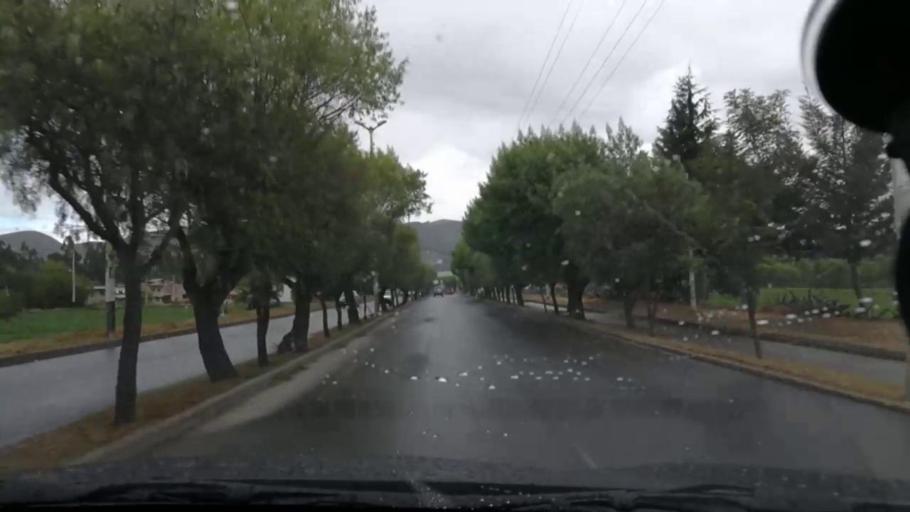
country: PE
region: Cajamarca
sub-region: Provincia de Cajamarca
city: Cajamarca
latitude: -7.1652
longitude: -78.4828
